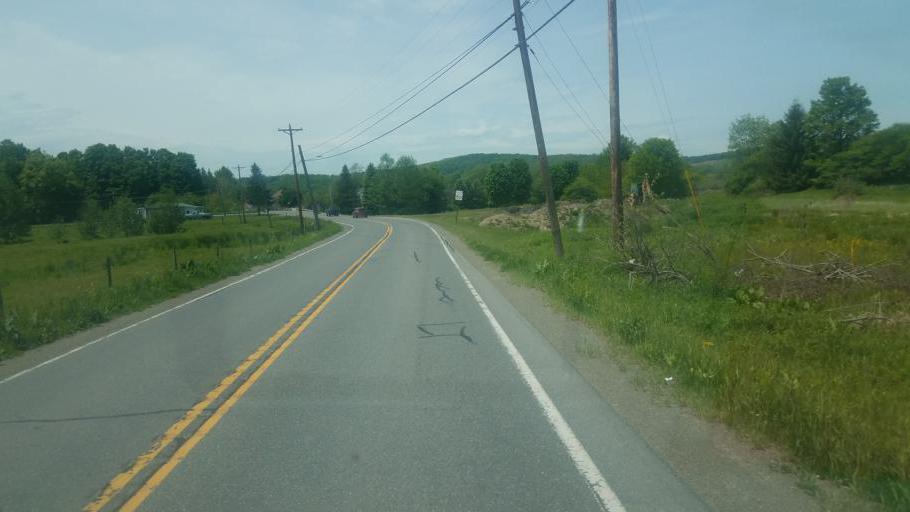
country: US
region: Pennsylvania
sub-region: Tioga County
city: Wellsboro
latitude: 41.7704
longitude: -77.2382
